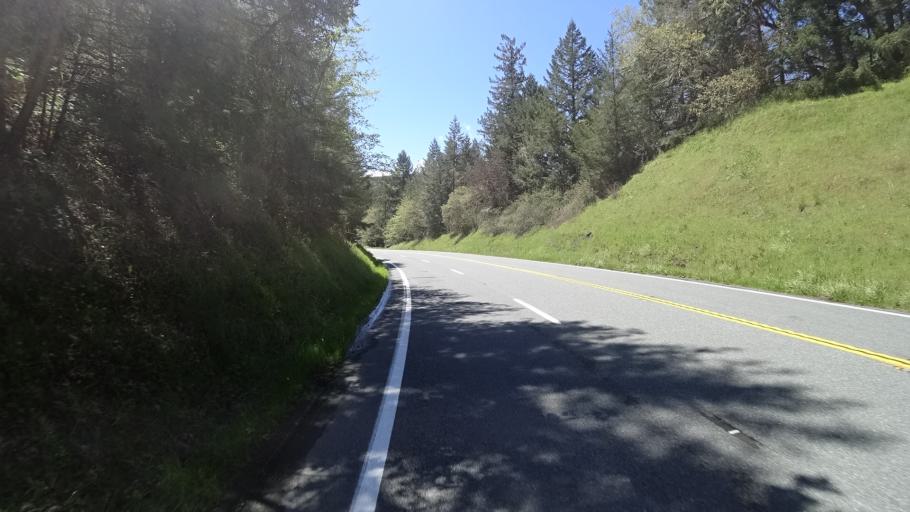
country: US
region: California
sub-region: Humboldt County
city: Blue Lake
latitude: 40.9125
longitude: -123.8086
